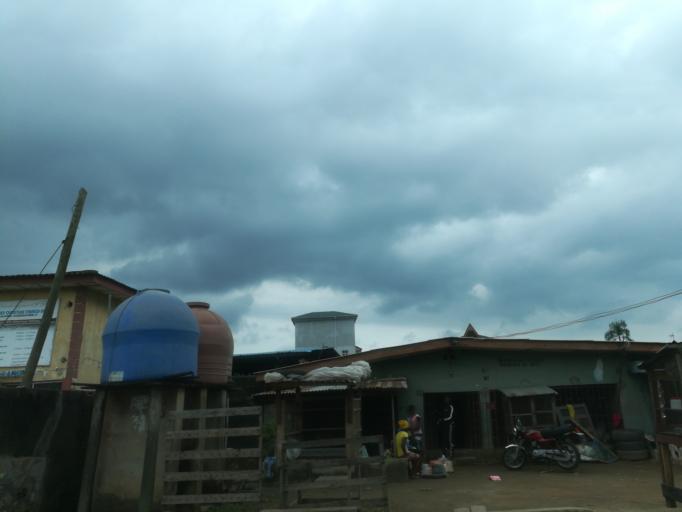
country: NG
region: Lagos
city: Oshodi
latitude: 6.5551
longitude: 3.3304
